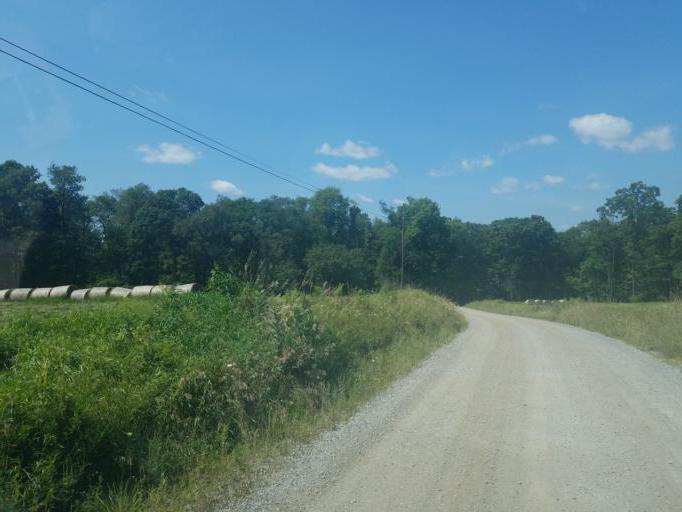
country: US
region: Pennsylvania
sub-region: Clarion County
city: Knox
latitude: 41.2016
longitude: -79.5585
